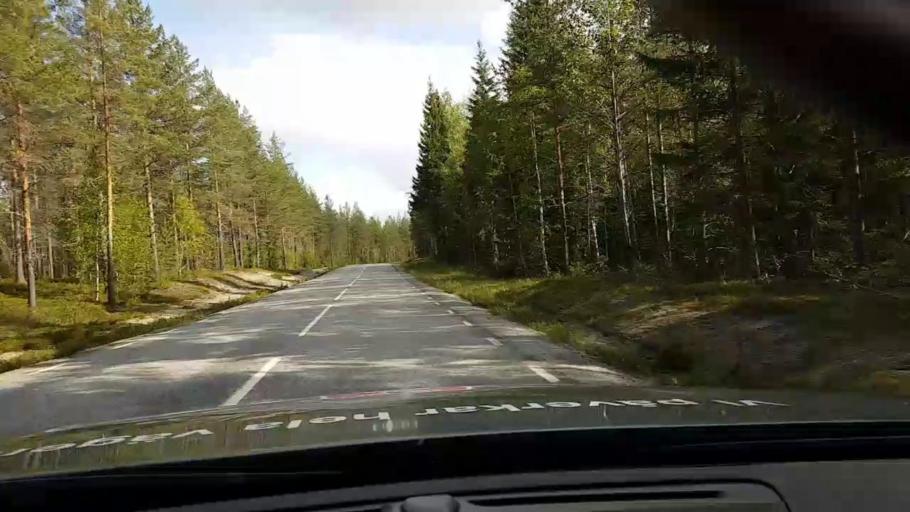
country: SE
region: Vaesternorrland
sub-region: OErnskoeldsviks Kommun
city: Bredbyn
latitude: 63.6539
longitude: 17.8824
